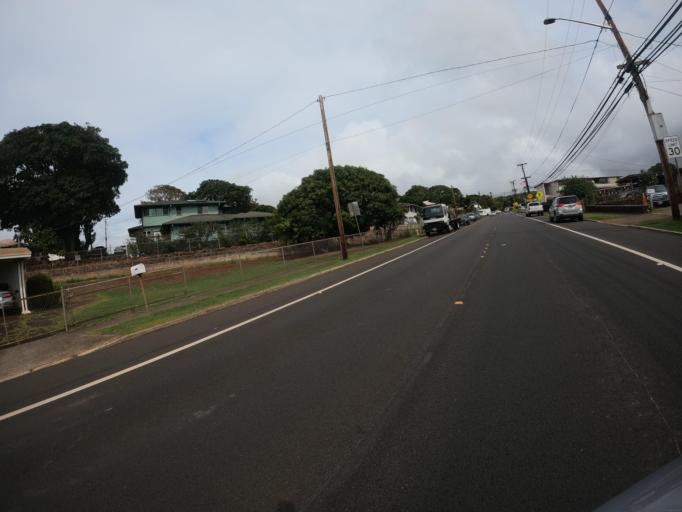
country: US
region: Hawaii
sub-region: Honolulu County
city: Halawa Heights
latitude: 21.3795
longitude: -157.9152
